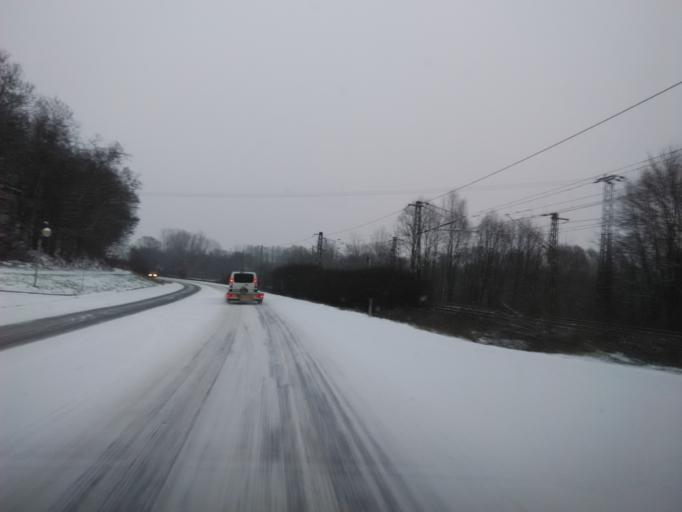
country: CZ
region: Olomoucky
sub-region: Okres Prerov
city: Hranice
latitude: 49.5268
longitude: 17.7532
